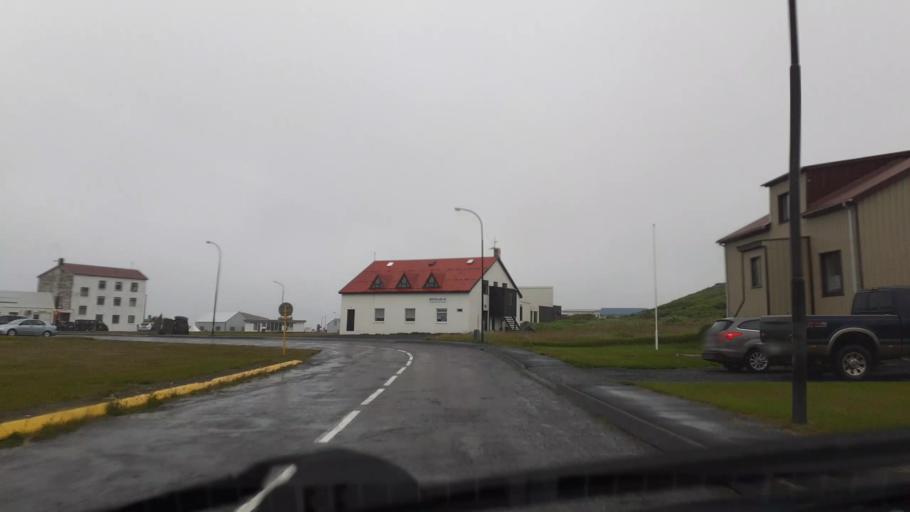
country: IS
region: Northeast
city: Husavik
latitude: 66.4546
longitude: -15.9525
